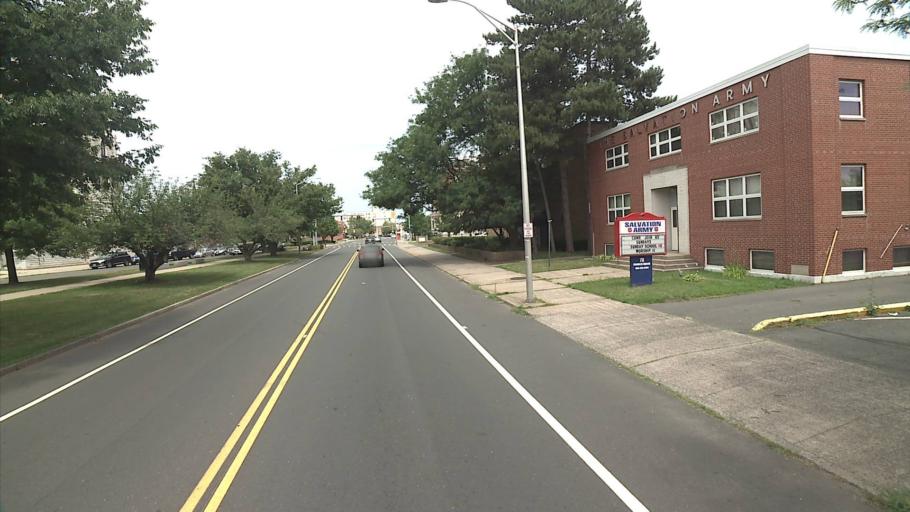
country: US
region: Connecticut
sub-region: Hartford County
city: New Britain
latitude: 41.6621
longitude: -72.7798
